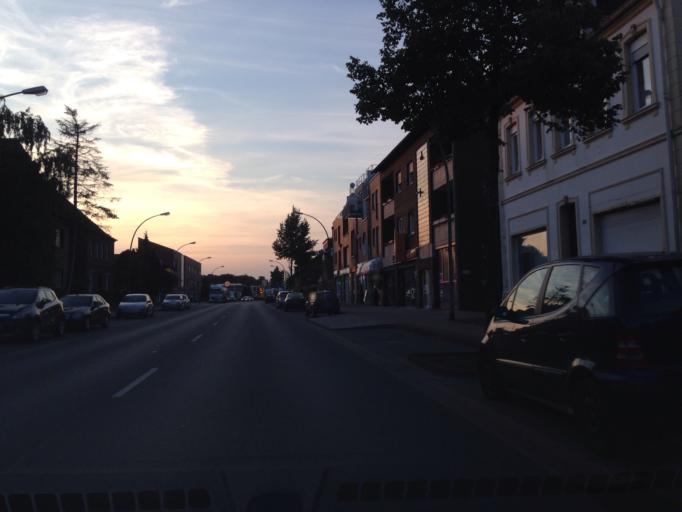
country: DE
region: North Rhine-Westphalia
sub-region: Regierungsbezirk Munster
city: Muenster
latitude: 51.9057
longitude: 7.6355
